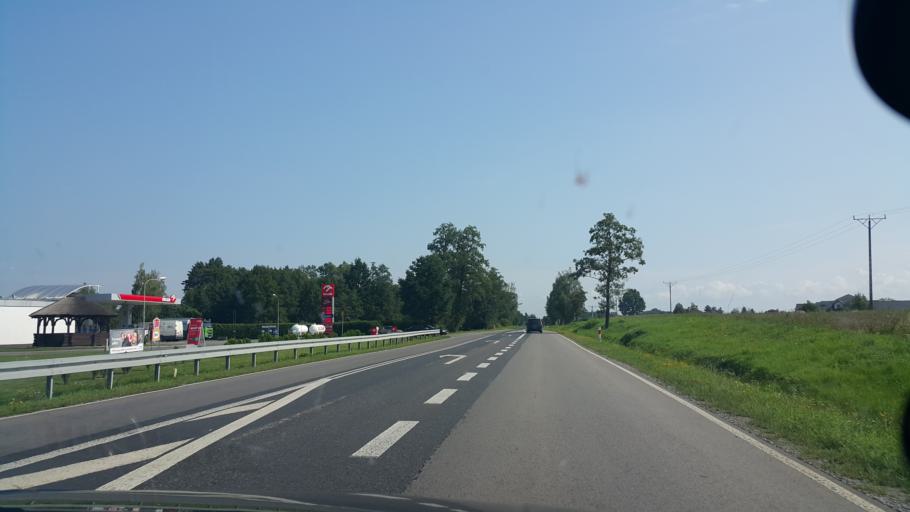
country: PL
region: Lublin Voivodeship
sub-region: Powiat leczynski
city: Cycow
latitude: 51.2942
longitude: 23.1118
